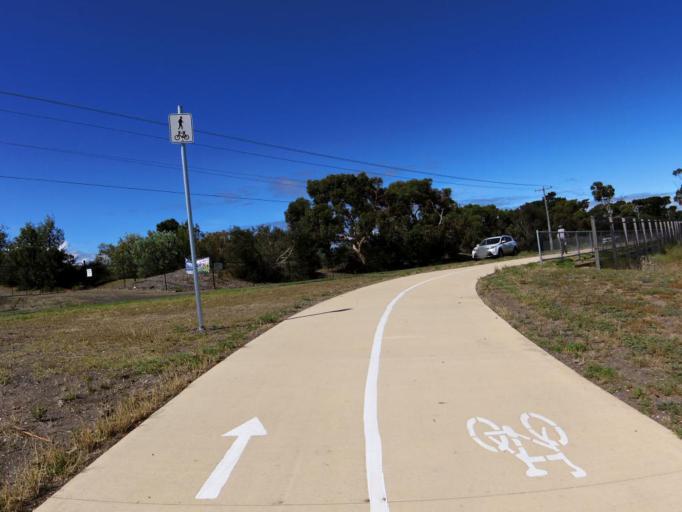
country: AU
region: Victoria
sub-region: Hobsons Bay
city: Altona Meadows
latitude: -37.8760
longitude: 144.7994
